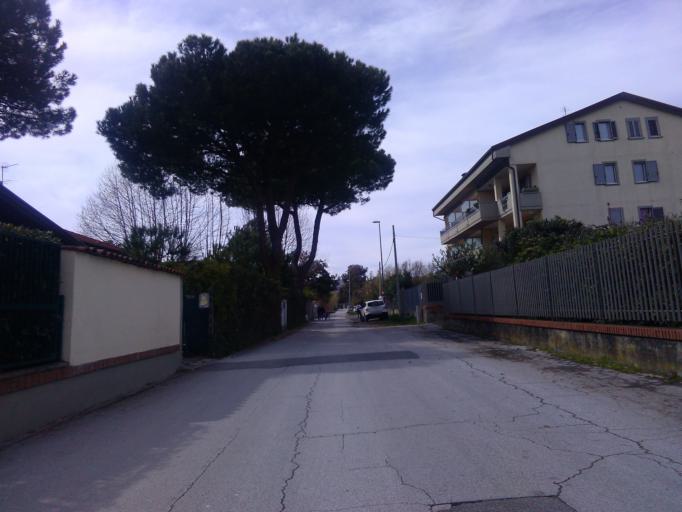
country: IT
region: Tuscany
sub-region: Provincia di Massa-Carrara
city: Marina di Carrara
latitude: 44.0477
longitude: 10.0251
